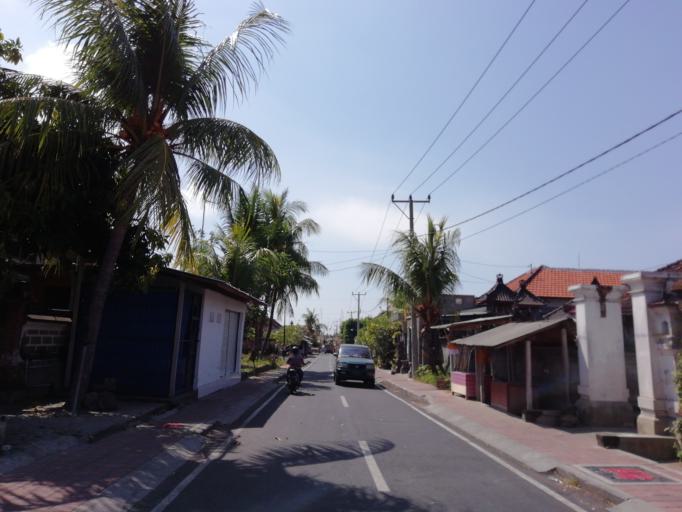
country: ID
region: Bali
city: Banjar Pasekan
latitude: -8.6107
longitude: 115.2840
